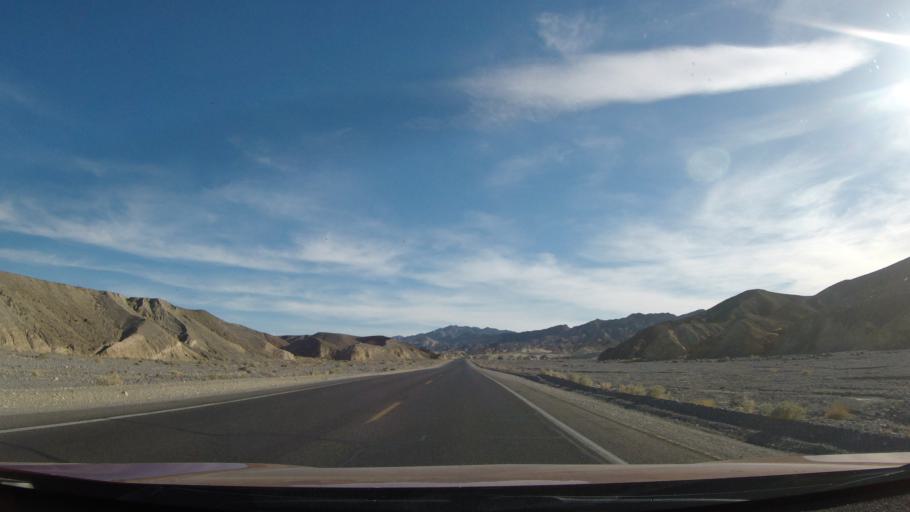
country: US
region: Nevada
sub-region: Nye County
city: Beatty
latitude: 36.4261
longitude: -116.8124
